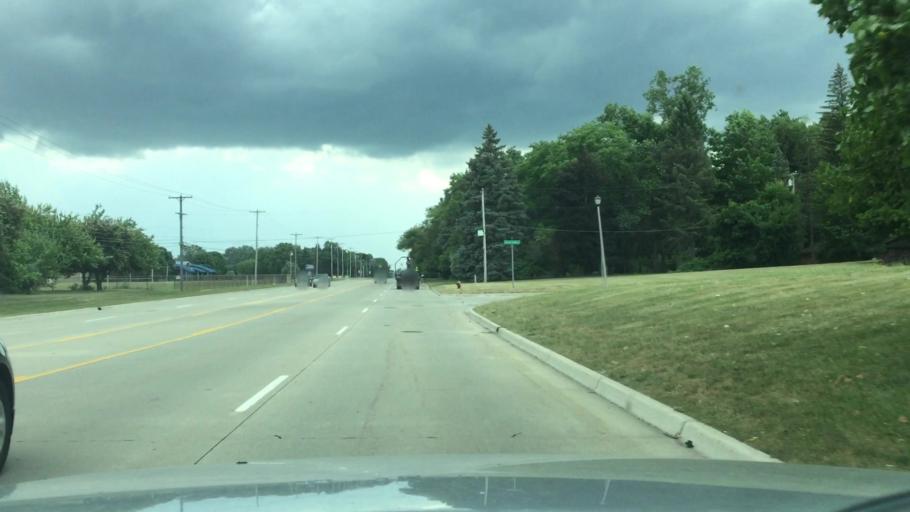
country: US
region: Michigan
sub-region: Genesee County
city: Flushing
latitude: 43.0285
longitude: -83.7735
